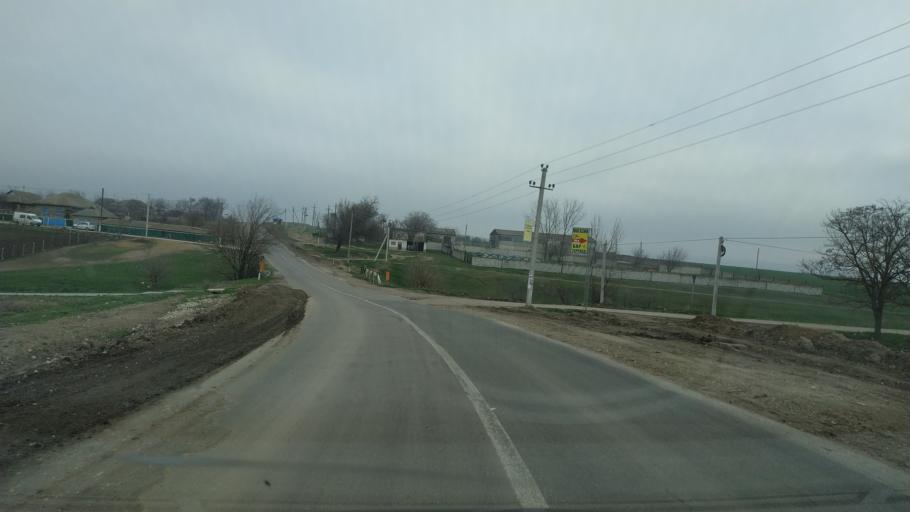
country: MD
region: Straseni
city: Taraclia
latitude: 45.9314
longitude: 28.5812
